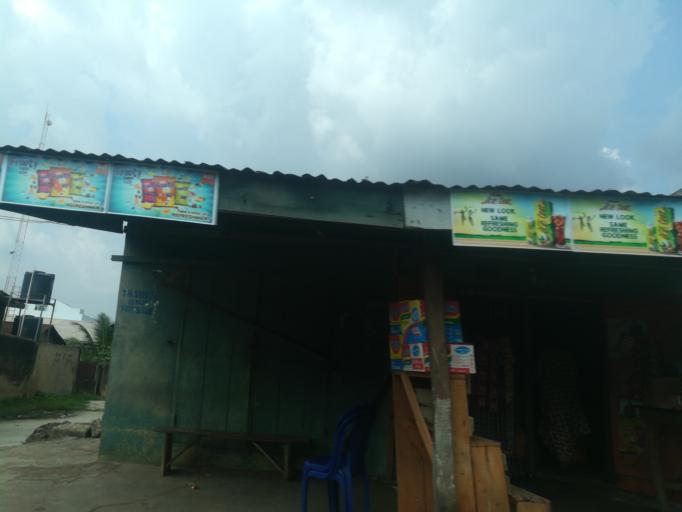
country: NG
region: Oyo
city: Ibadan
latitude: 7.3480
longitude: 3.8771
